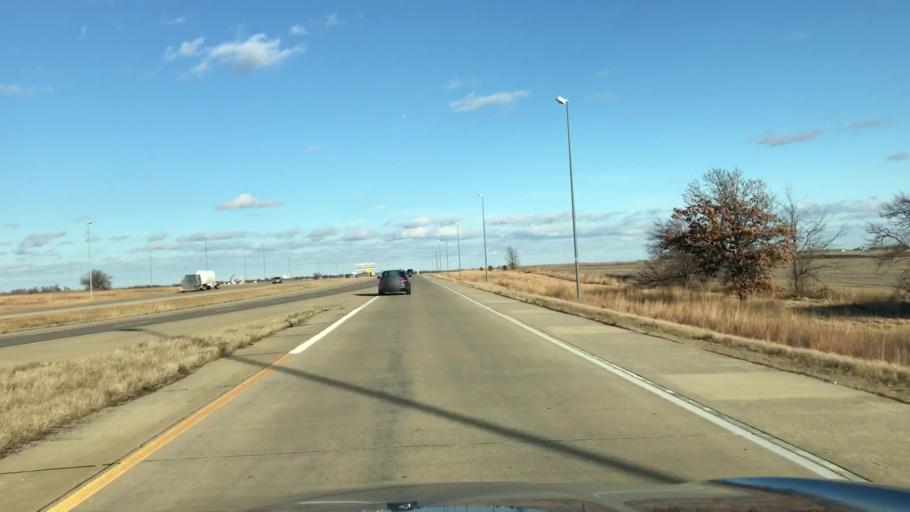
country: US
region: Illinois
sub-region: McLean County
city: Normal
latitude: 40.5378
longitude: -88.9435
